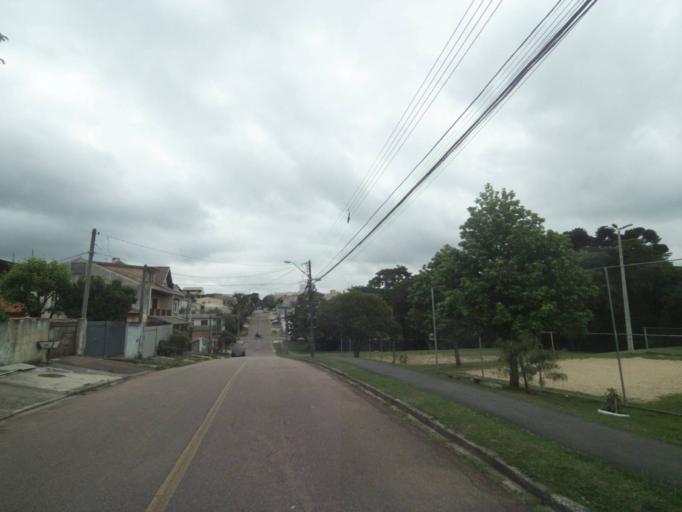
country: BR
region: Parana
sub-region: Sao Jose Dos Pinhais
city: Sao Jose dos Pinhais
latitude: -25.5454
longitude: -49.2693
